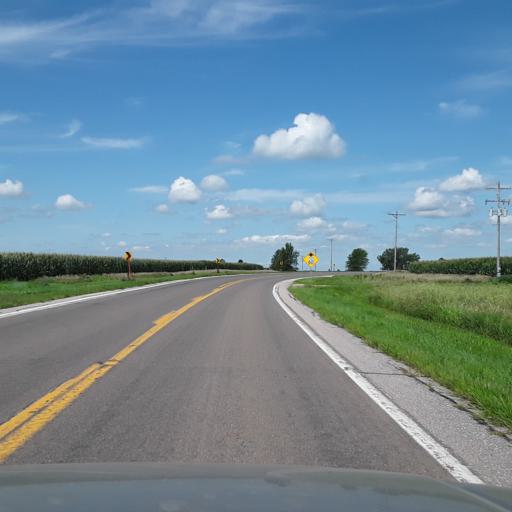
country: US
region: Nebraska
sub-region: Polk County
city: Osceola
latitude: 41.0758
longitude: -97.4205
